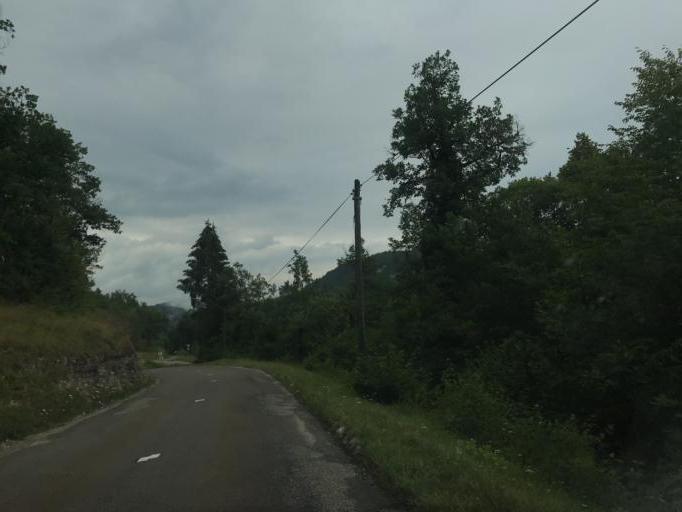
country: FR
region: Franche-Comte
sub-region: Departement du Jura
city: Lavans-les-Saint-Claude
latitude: 46.3215
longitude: 5.7565
